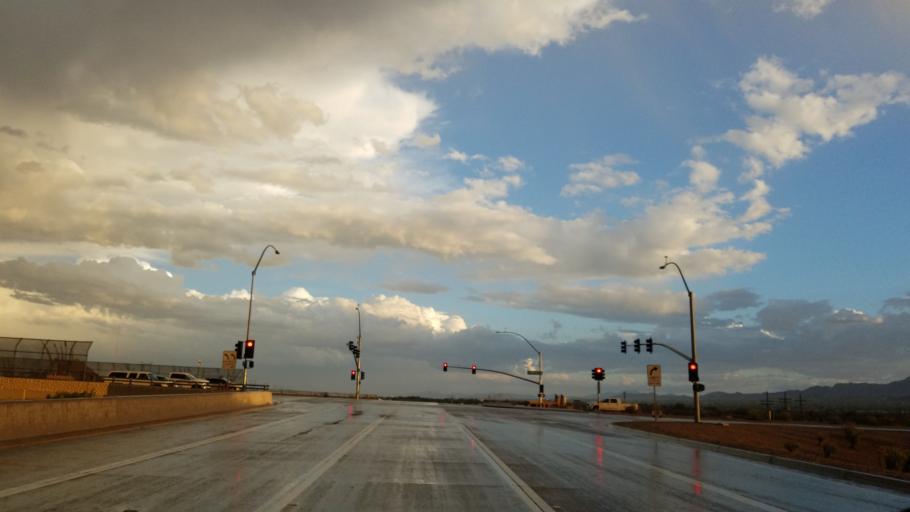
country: US
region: Arizona
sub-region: Pima County
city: Tortolita
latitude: 32.3792
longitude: -111.1106
